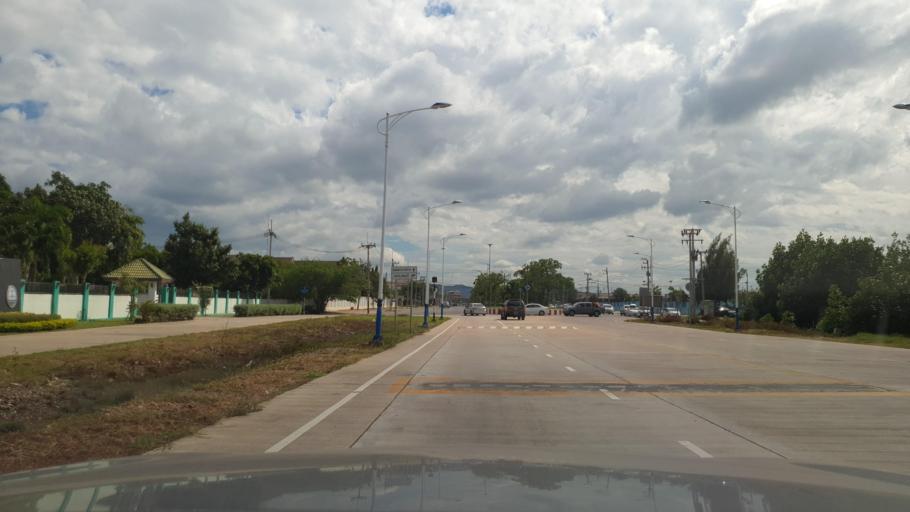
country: TH
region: Chon Buri
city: Chon Buri
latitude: 13.3452
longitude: 100.9496
